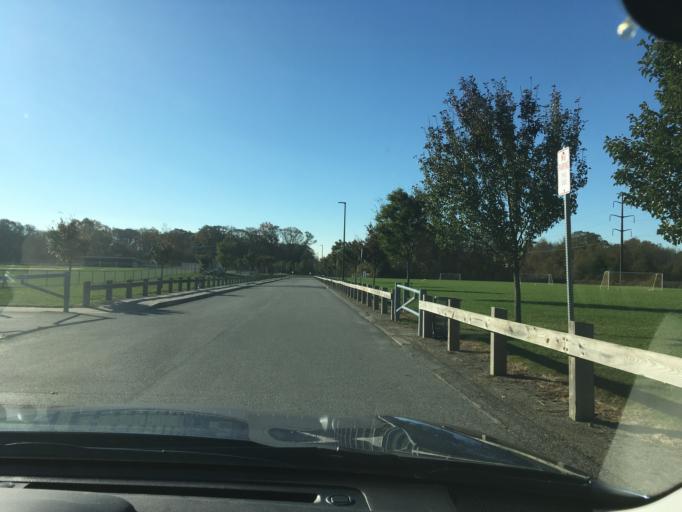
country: US
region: Rhode Island
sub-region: Kent County
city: East Greenwich
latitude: 41.6367
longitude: -71.4854
